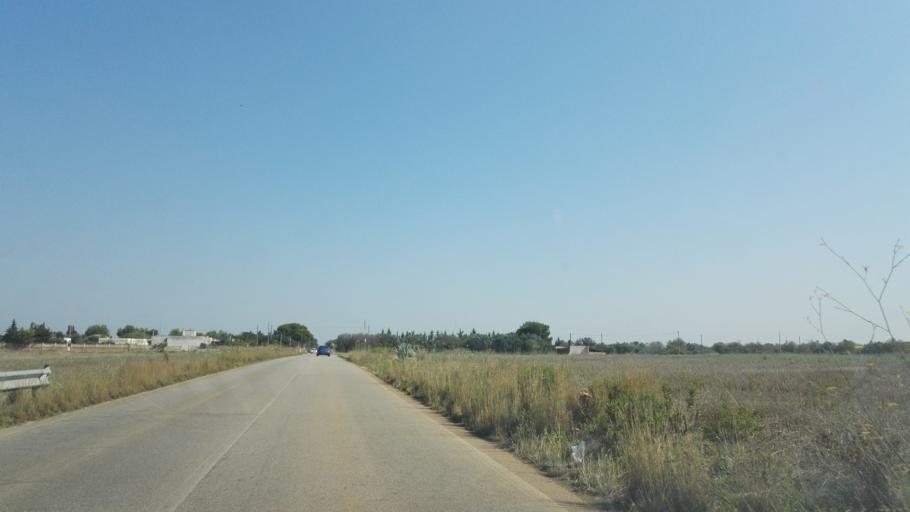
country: IT
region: Apulia
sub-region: Provincia di Lecce
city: Nardo
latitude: 40.1160
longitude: 18.0201
